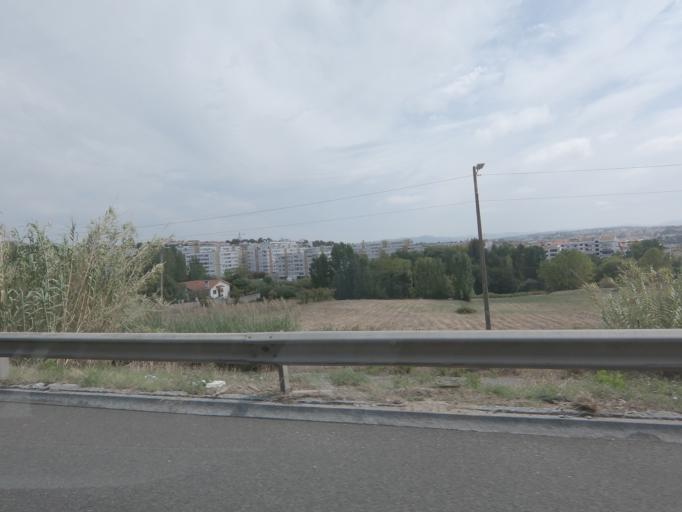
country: PT
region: Leiria
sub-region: Leiria
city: Leiria
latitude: 39.7602
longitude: -8.8060
